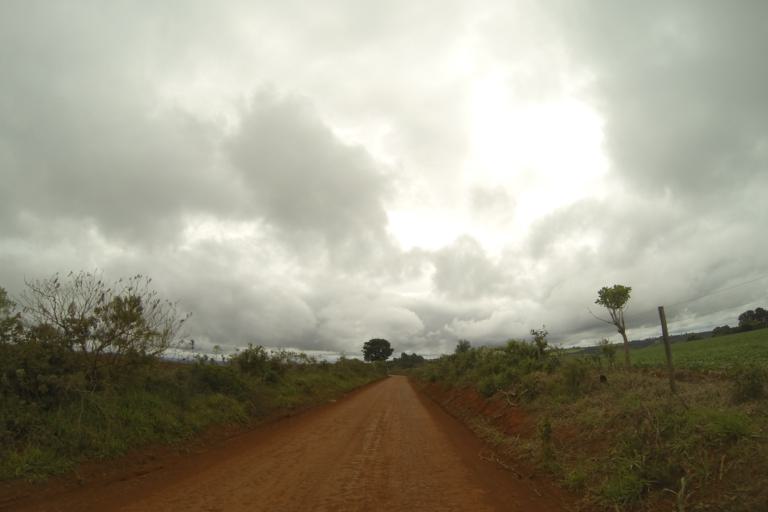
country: BR
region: Minas Gerais
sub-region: Campos Altos
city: Campos Altos
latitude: -19.8581
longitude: -46.3119
